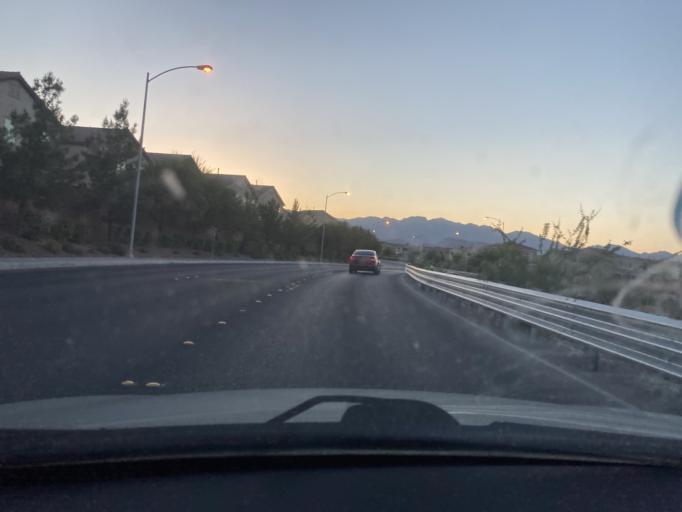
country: US
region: Nevada
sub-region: Clark County
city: Enterprise
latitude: 36.0615
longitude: -115.2854
